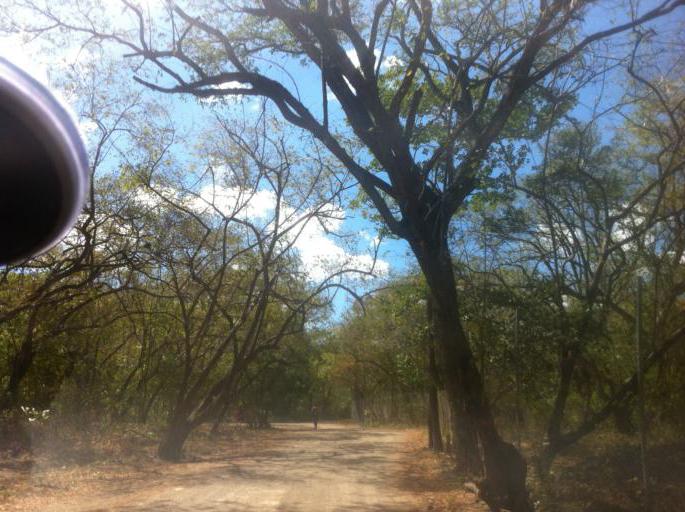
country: NI
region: Rivas
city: Tola
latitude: 11.3839
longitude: -86.0233
